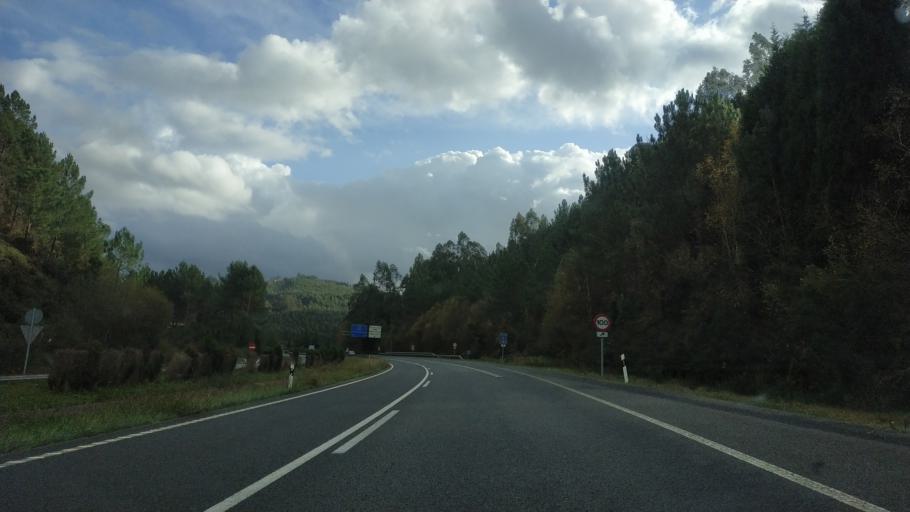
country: ES
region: Galicia
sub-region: Provincia da Coruna
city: Abegondo
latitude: 43.2521
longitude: -8.2943
